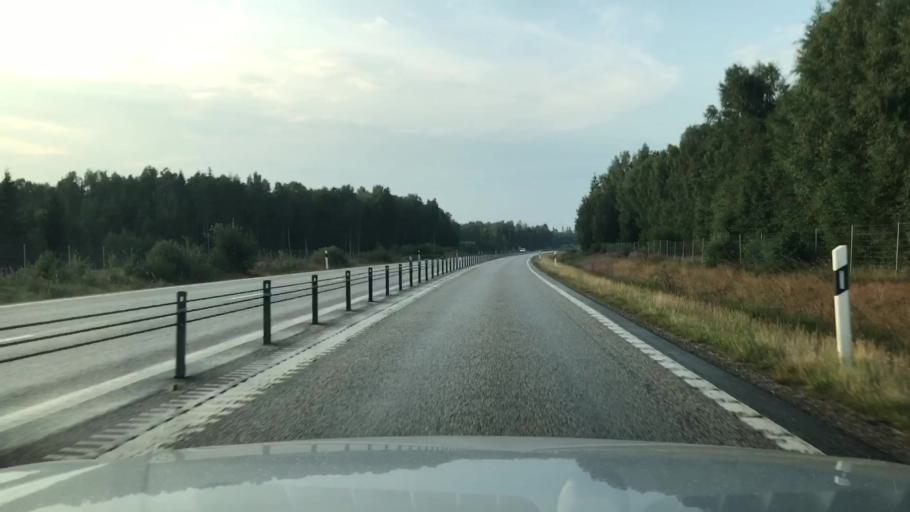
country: SE
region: Kronoberg
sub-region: Ljungby Kommun
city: Lagan
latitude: 57.0141
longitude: 14.0393
